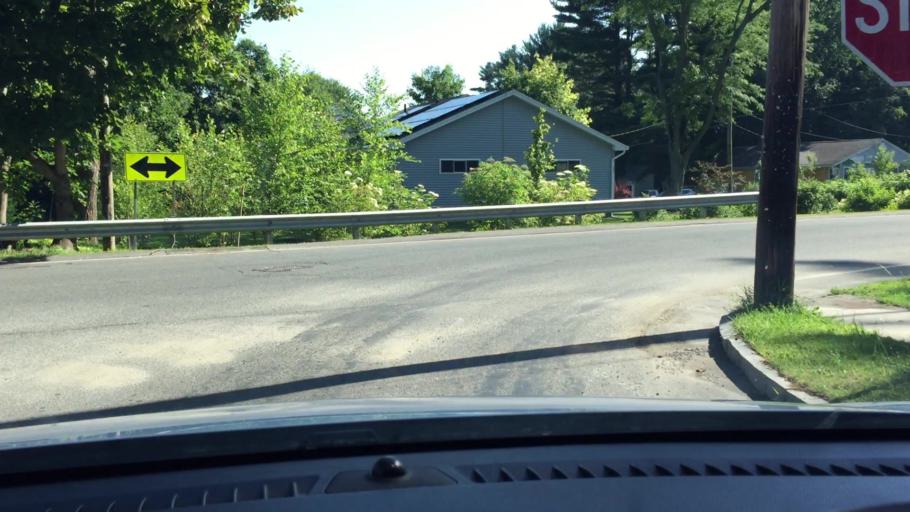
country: US
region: Massachusetts
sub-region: Berkshire County
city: Pittsfield
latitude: 42.4873
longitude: -73.2586
